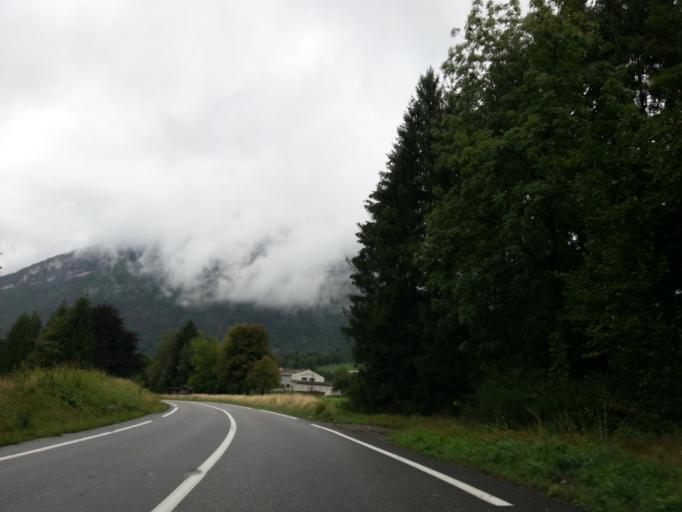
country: FR
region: Rhone-Alpes
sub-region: Departement de la Savoie
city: Ugine
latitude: 45.7551
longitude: 6.4021
